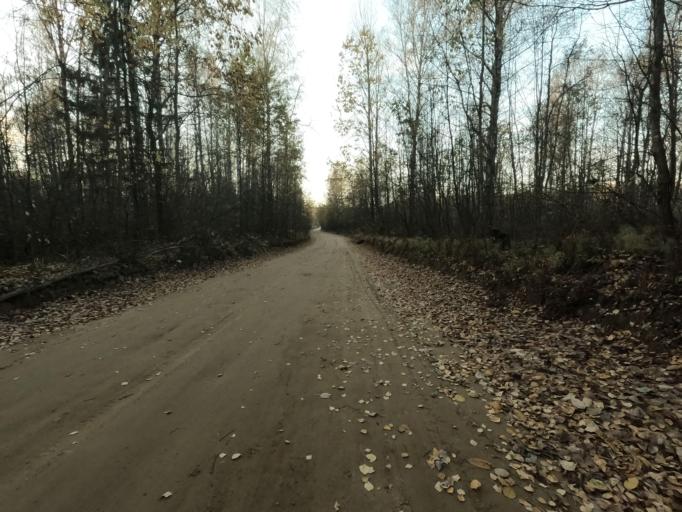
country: RU
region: Leningrad
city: Mga
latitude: 59.7550
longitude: 31.2805
